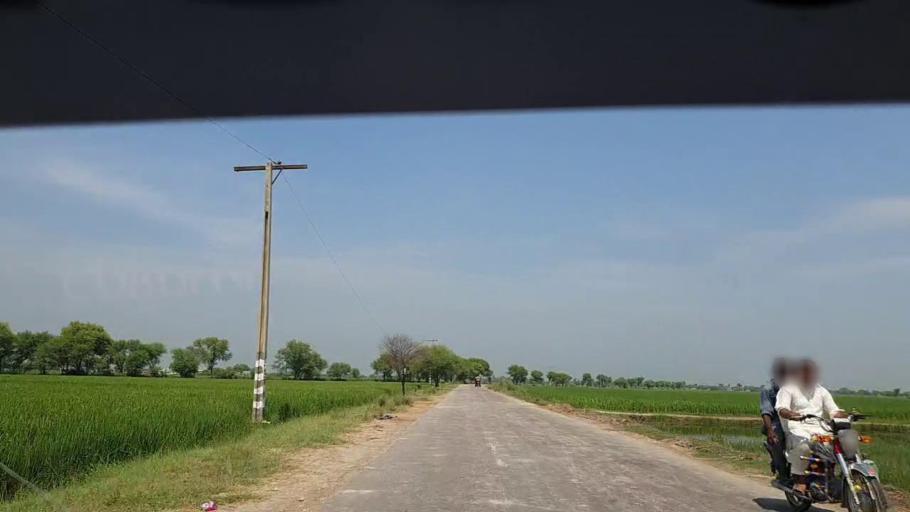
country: PK
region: Sindh
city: Thul
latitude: 28.1385
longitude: 68.7161
